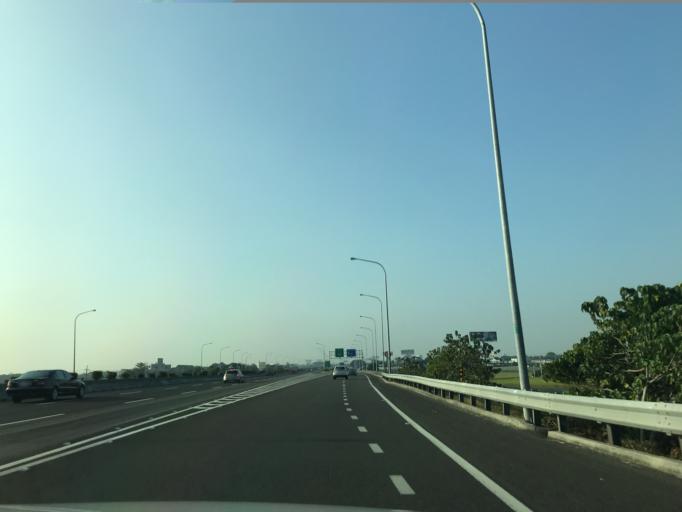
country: TW
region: Taiwan
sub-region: Yunlin
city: Douliu
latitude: 23.7943
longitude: 120.4804
